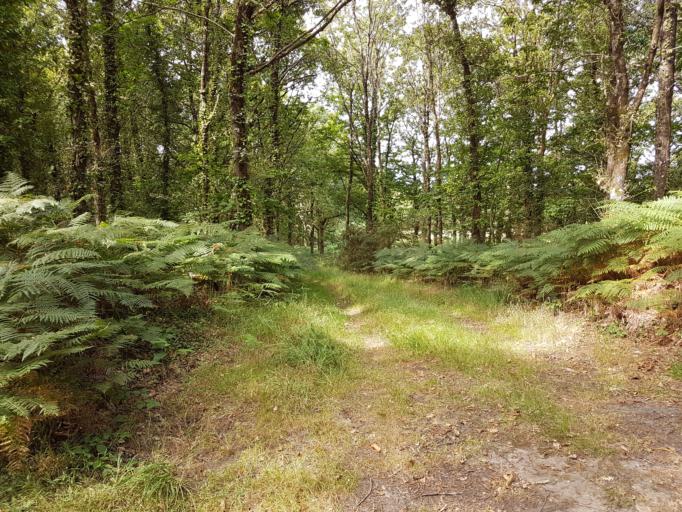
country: FR
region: Brittany
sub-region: Departement du Morbihan
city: Sainte-Helene
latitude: 47.7118
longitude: -3.2010
